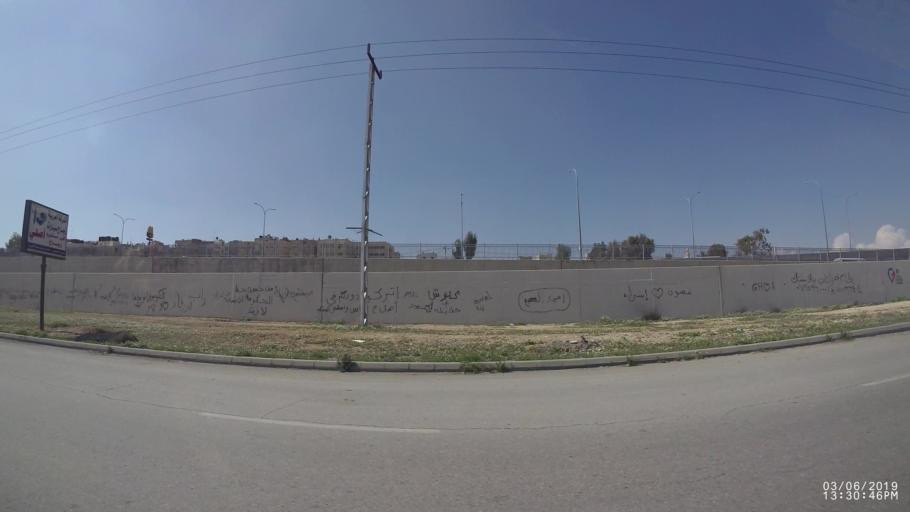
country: JO
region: Zarqa
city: Zarqa
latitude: 32.0789
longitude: 36.1060
